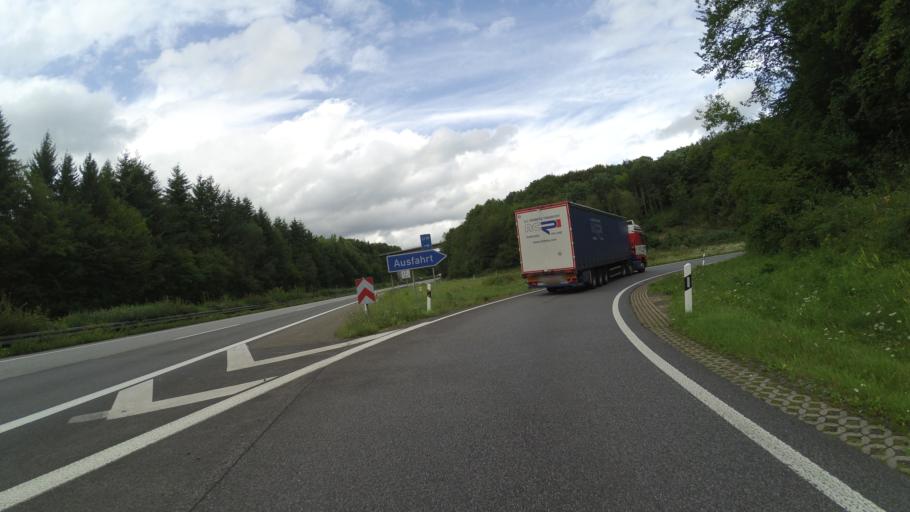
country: DE
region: Saarland
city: Tholey
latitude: 49.4899
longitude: 6.9873
